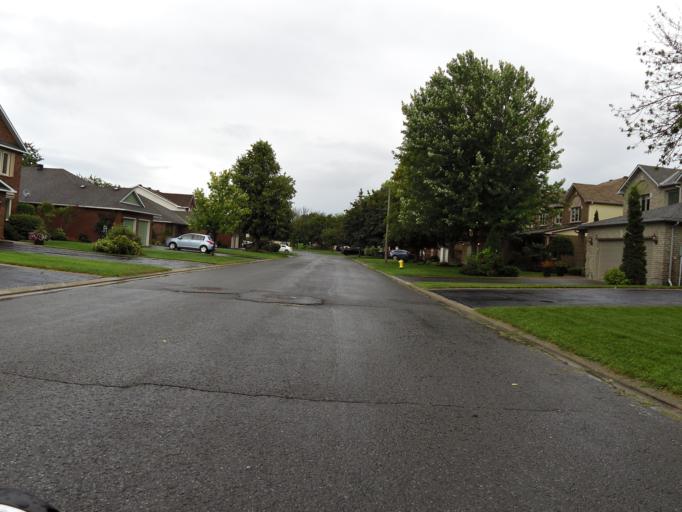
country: CA
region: Ontario
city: Bells Corners
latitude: 45.3268
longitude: -75.9150
